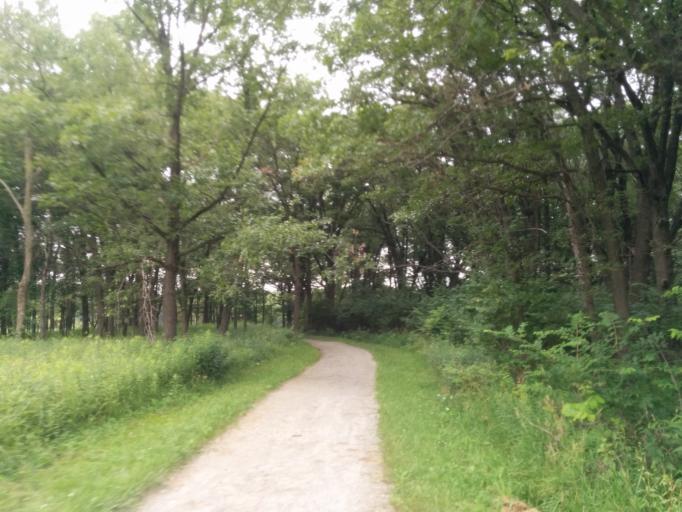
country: US
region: Illinois
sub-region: Cook County
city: Willow Springs
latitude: 41.7047
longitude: -87.8816
